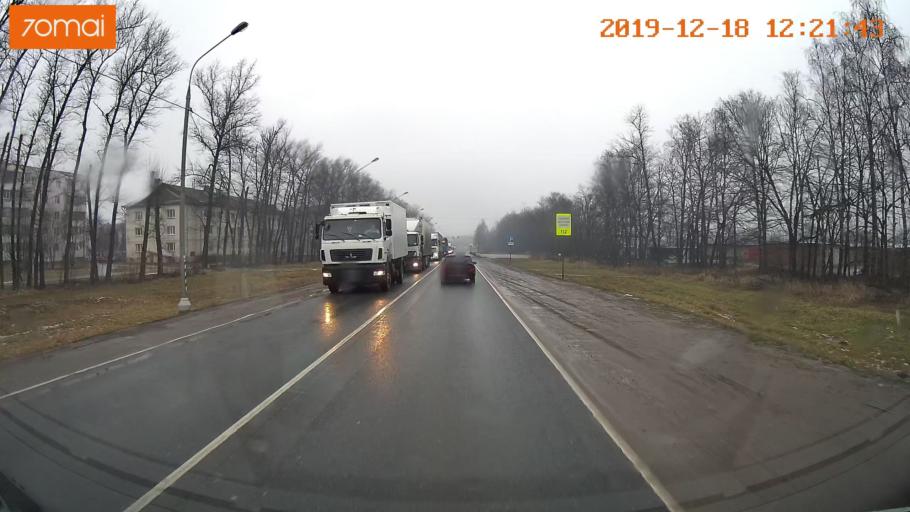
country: RU
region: Moskovskaya
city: Novopetrovskoye
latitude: 56.0002
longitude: 36.4757
